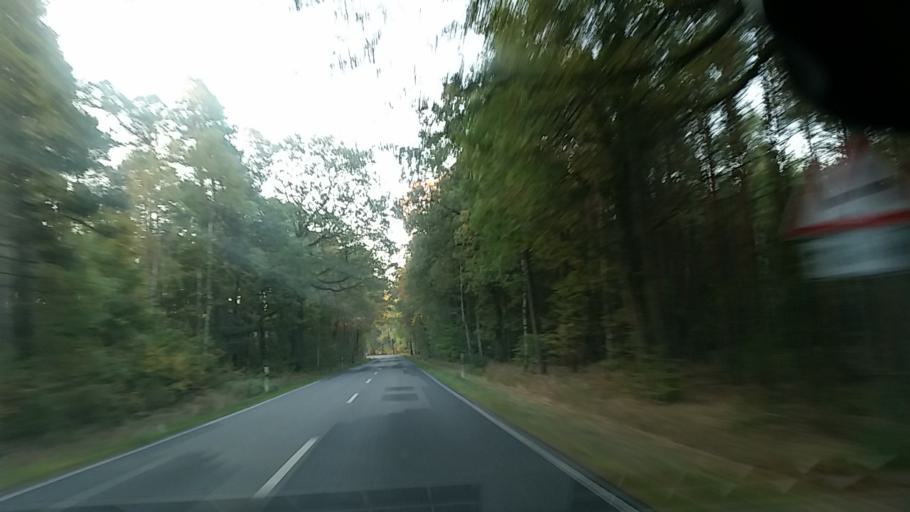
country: DE
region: Lower Saxony
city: Tulau
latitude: 52.6347
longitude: 10.8106
